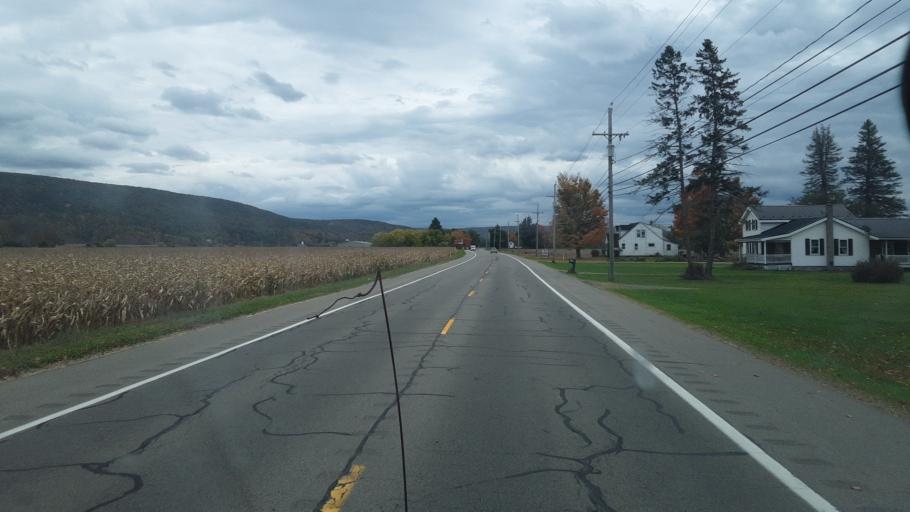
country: US
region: New York
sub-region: Allegany County
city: Belmont
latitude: 42.2069
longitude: -78.0115
